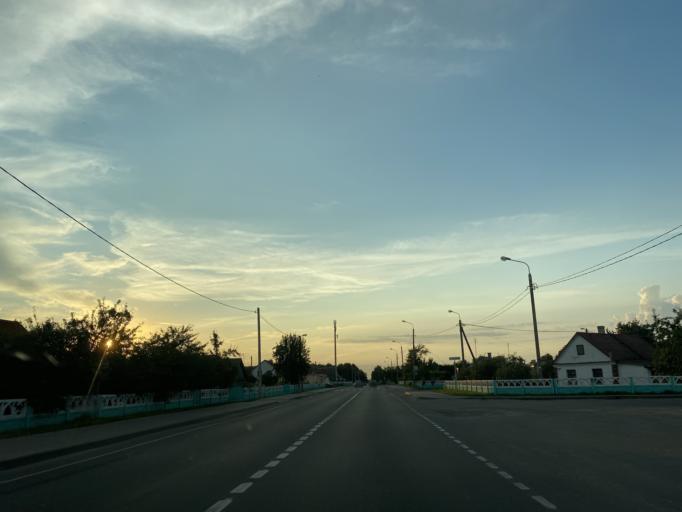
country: BY
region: Brest
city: Ivatsevichy
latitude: 52.7098
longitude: 25.3533
